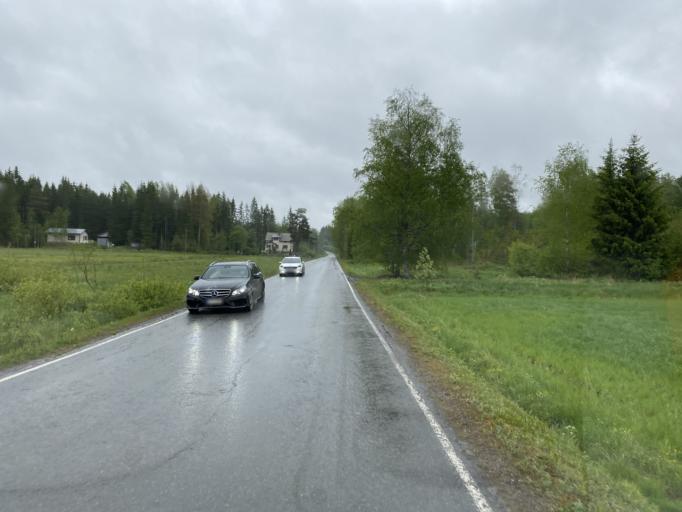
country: FI
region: Pirkanmaa
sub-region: Etelae-Pirkanmaa
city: Urjala
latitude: 60.9651
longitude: 23.5174
